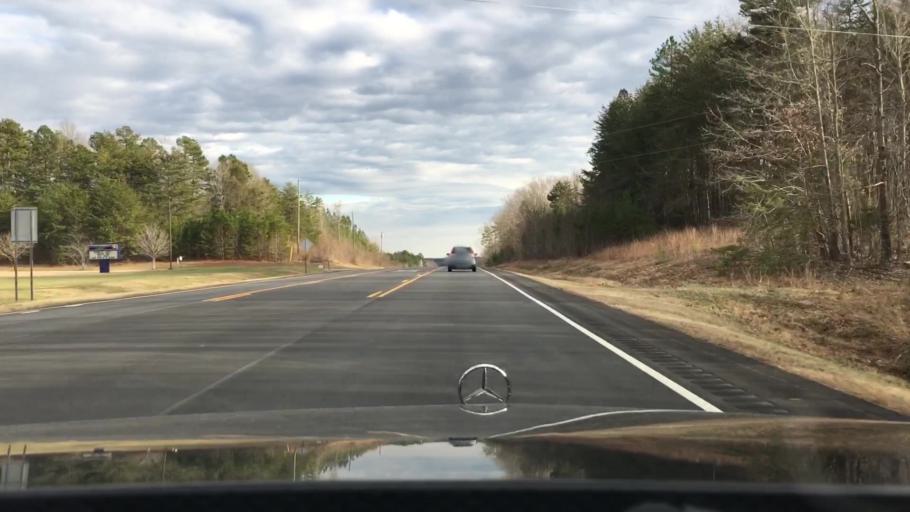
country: US
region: North Carolina
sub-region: Caswell County
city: Yanceyville
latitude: 36.3275
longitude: -79.2410
